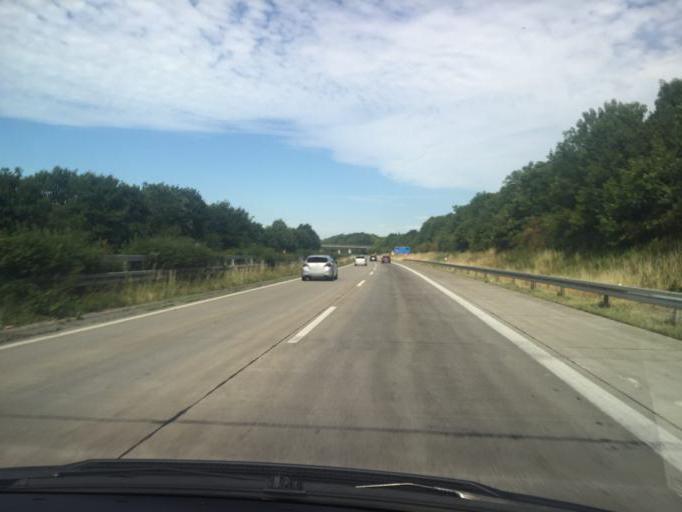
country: DE
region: North Rhine-Westphalia
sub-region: Regierungsbezirk Dusseldorf
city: Goch
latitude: 51.6733
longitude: 6.1131
